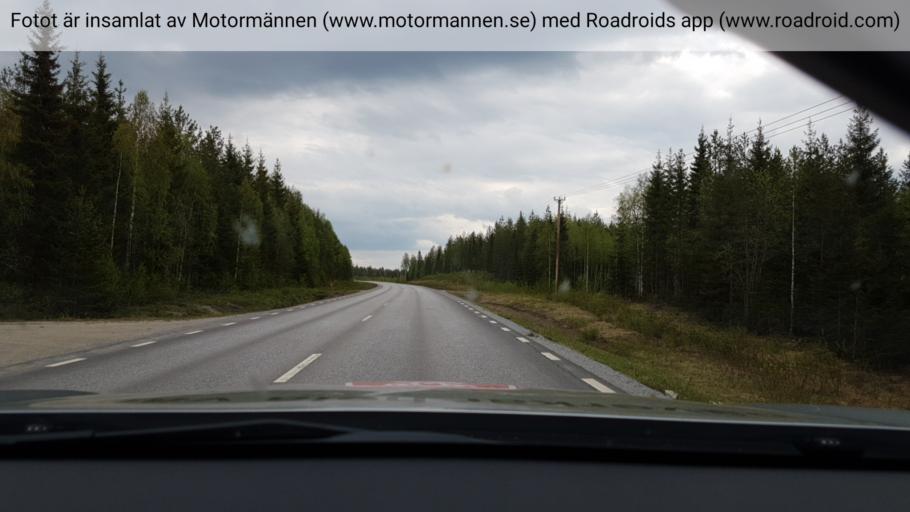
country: SE
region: Vaesterbotten
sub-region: Vannas Kommun
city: Vaennaes
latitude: 63.9279
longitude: 19.5243
